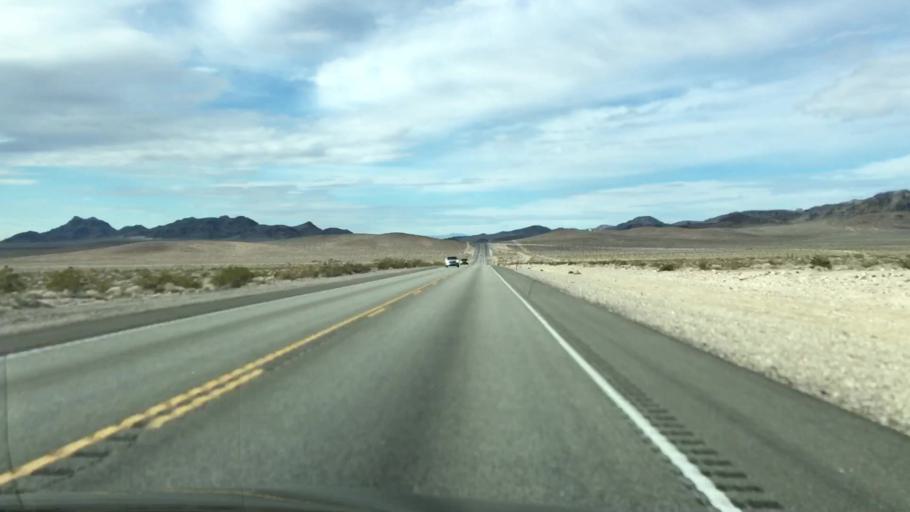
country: US
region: Nevada
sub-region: Nye County
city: Pahrump
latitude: 36.6048
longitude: -116.2573
